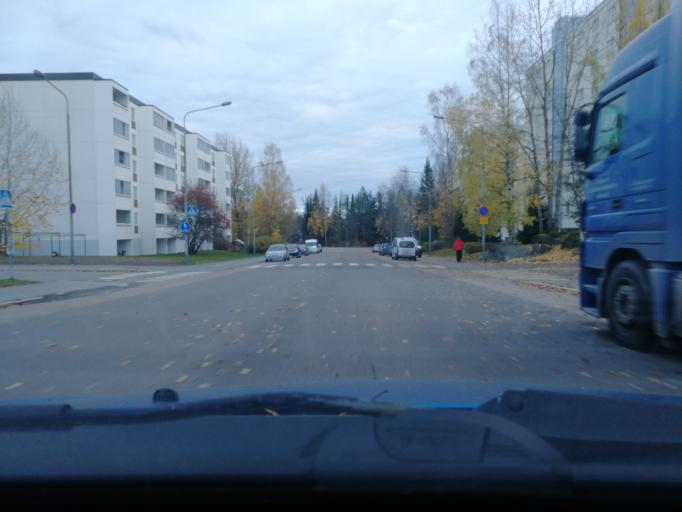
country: FI
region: Pirkanmaa
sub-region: Tampere
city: Tampere
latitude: 61.4525
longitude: 23.8370
